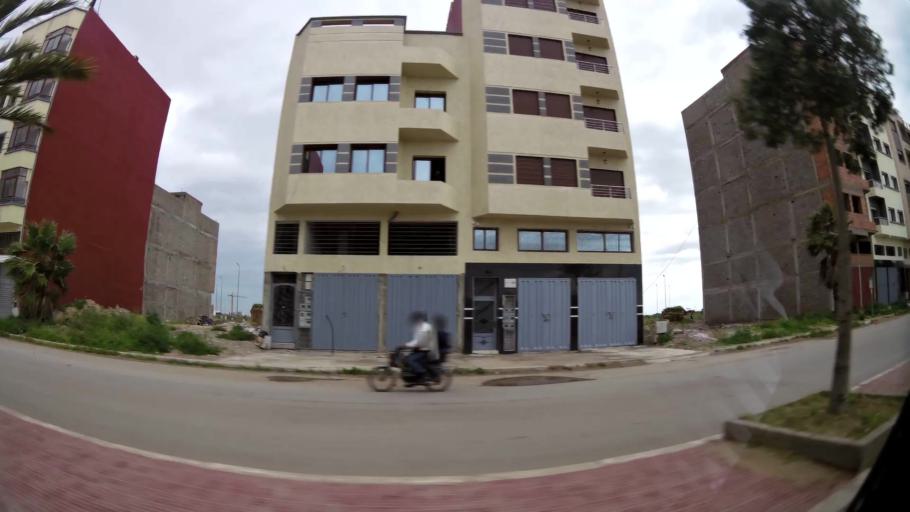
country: MA
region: Grand Casablanca
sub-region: Mediouna
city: Tit Mellil
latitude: 33.5523
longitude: -7.5324
